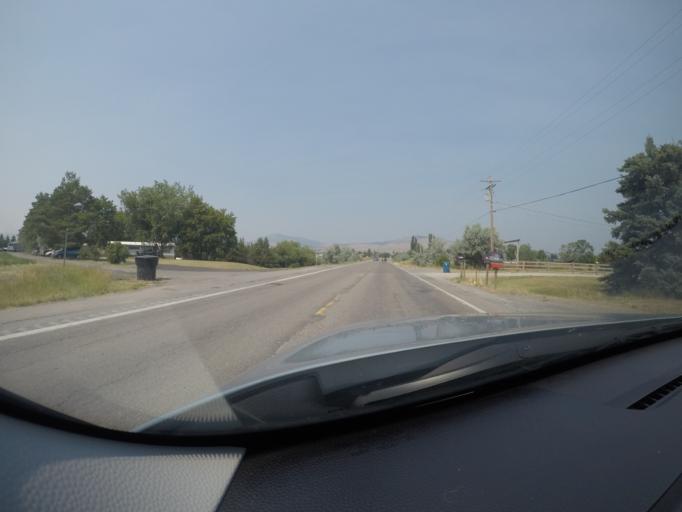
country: US
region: Montana
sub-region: Lake County
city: Polson
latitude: 47.7116
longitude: -114.1867
